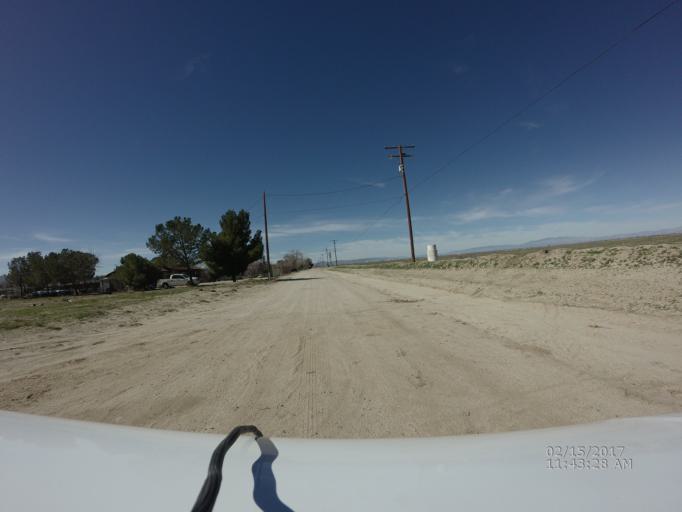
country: US
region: California
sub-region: Los Angeles County
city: Littlerock
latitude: 34.5871
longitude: -117.9548
